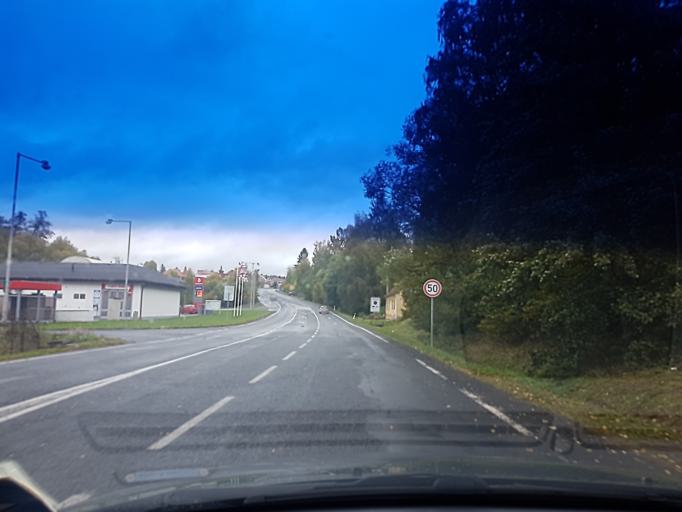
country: CZ
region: Karlovarsky
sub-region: Okres Cheb
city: Cheb
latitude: 50.0723
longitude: 12.3607
